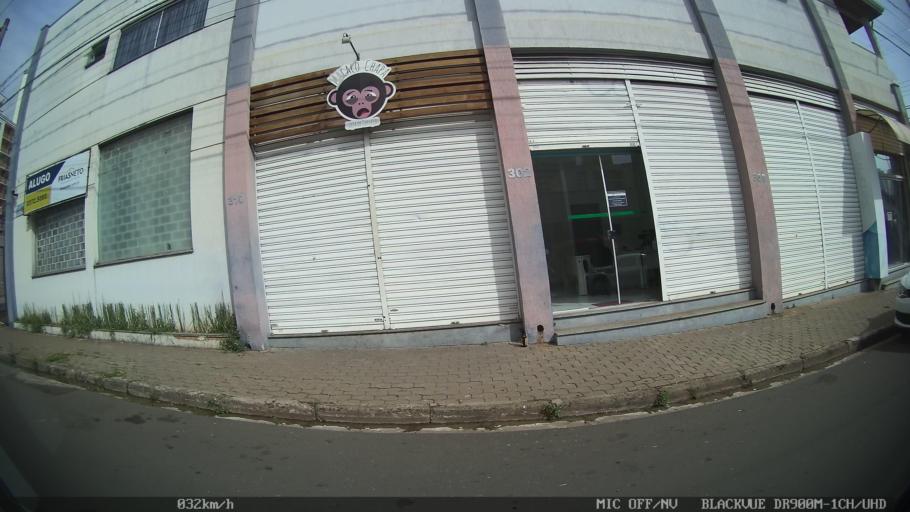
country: BR
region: Sao Paulo
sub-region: Piracicaba
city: Piracicaba
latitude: -22.7250
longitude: -47.6545
